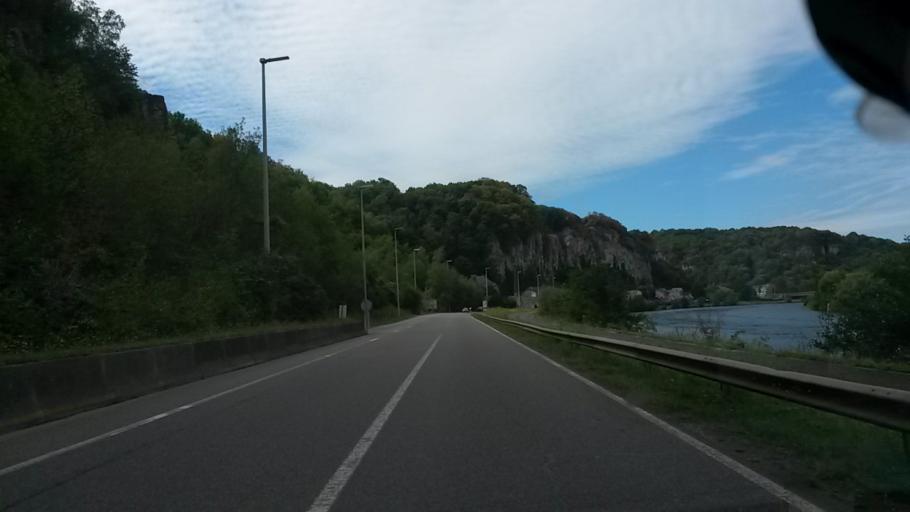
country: BE
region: Wallonia
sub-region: Province de Namur
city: Noville-les-Bois
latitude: 50.4706
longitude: 5.0059
